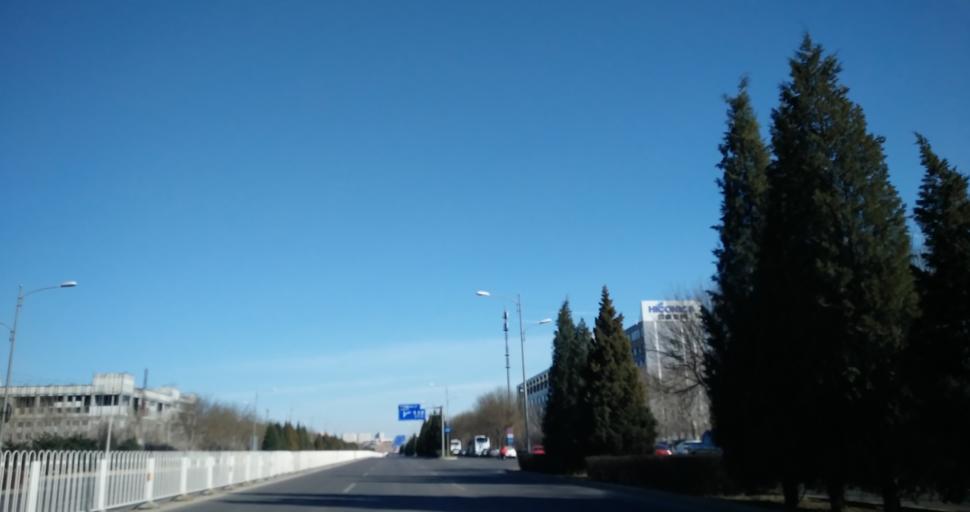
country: CN
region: Beijing
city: Qingyundian
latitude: 39.7559
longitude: 116.5187
